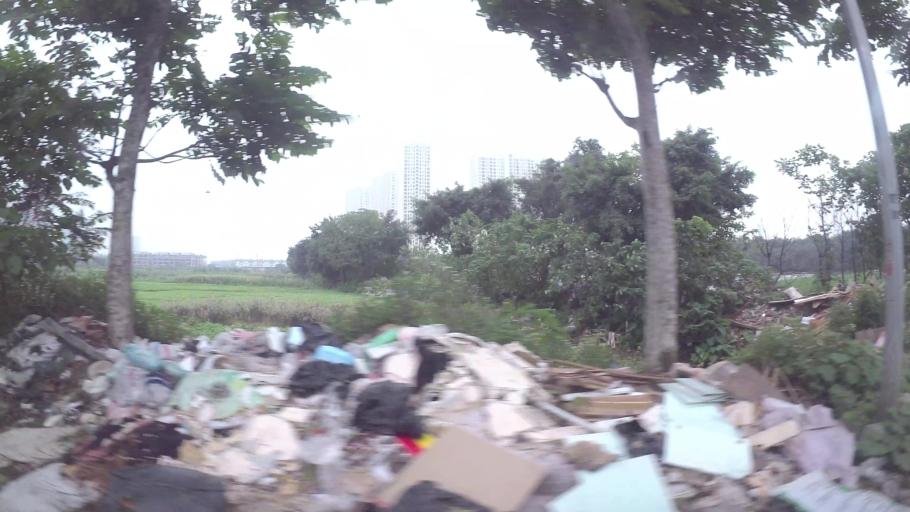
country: VN
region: Ha Noi
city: Hai BaTrung
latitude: 20.9795
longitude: 105.8699
